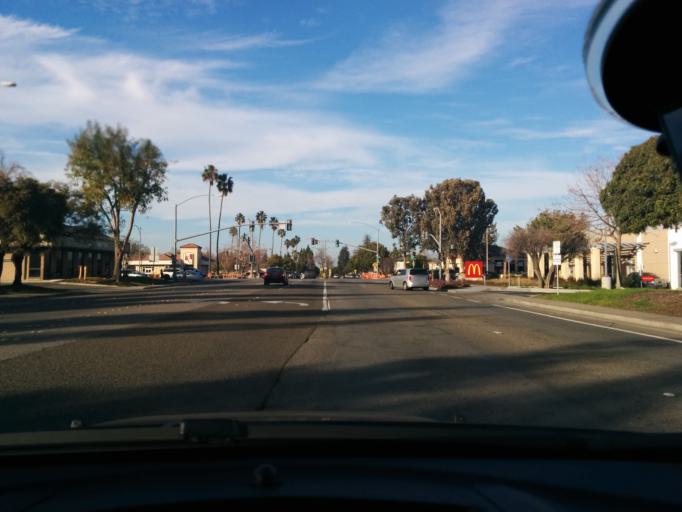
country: US
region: California
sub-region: Santa Clara County
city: Cupertino
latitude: 37.3366
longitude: -122.0414
